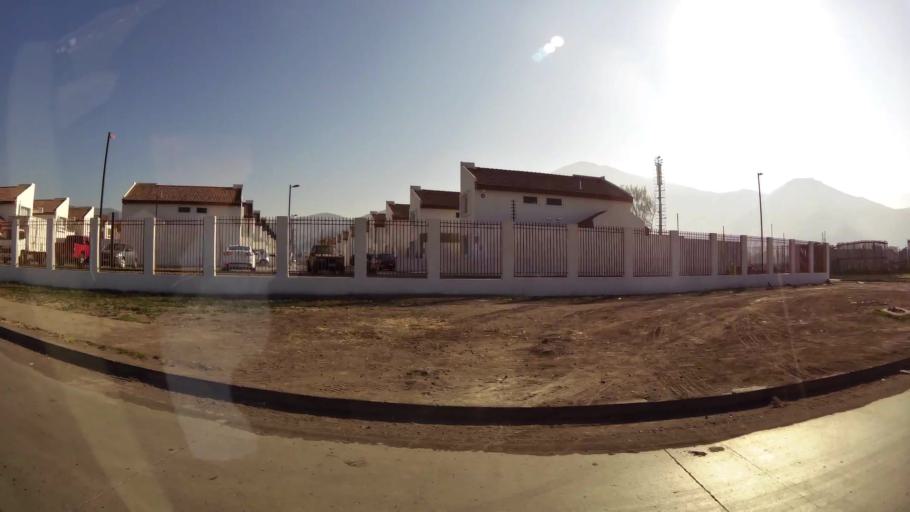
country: CL
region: Santiago Metropolitan
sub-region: Provincia de Chacabuco
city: Chicureo Abajo
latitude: -33.3651
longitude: -70.6652
